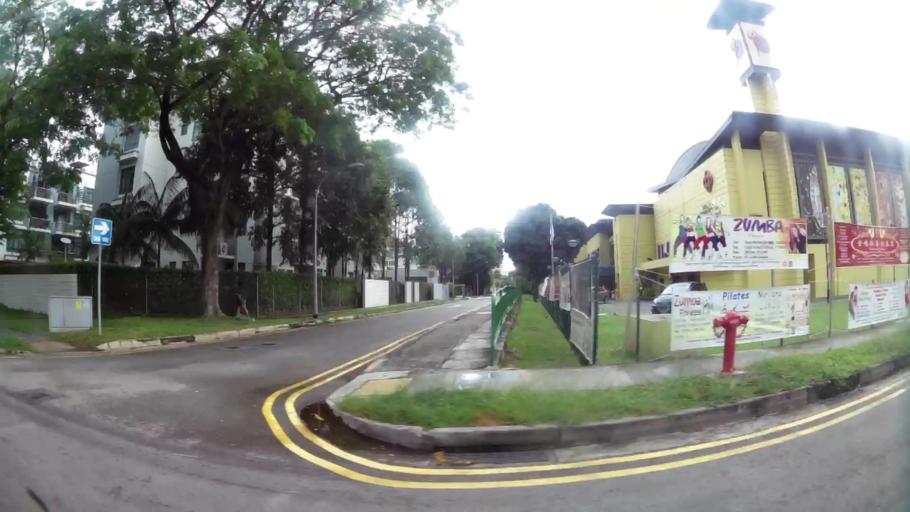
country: SG
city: Singapore
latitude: 1.3137
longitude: 103.9309
